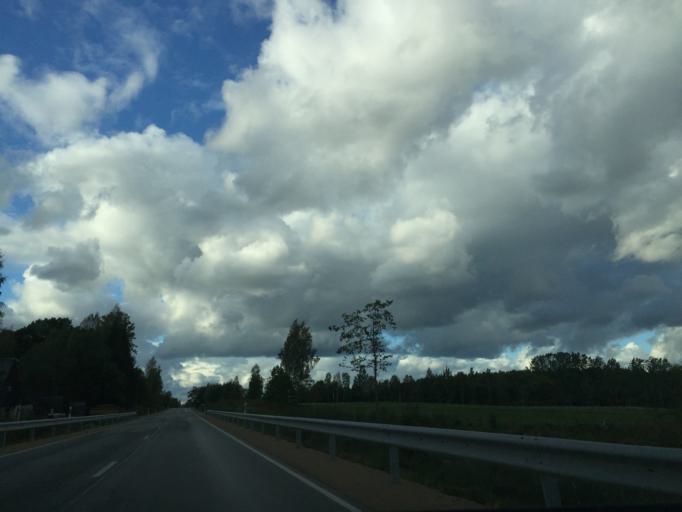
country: LV
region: Ligatne
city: Ligatne
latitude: 57.1690
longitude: 25.0458
